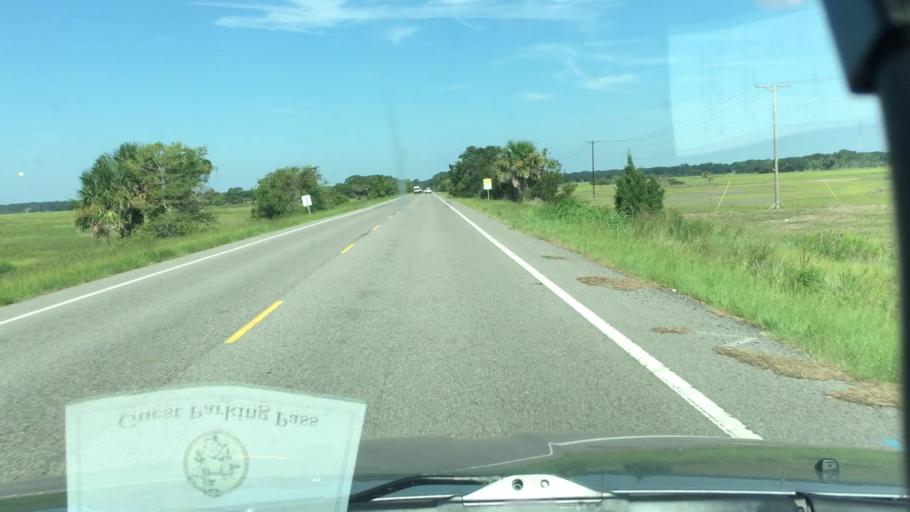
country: US
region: South Carolina
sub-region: Beaufort County
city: Beaufort
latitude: 32.4074
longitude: -80.4619
